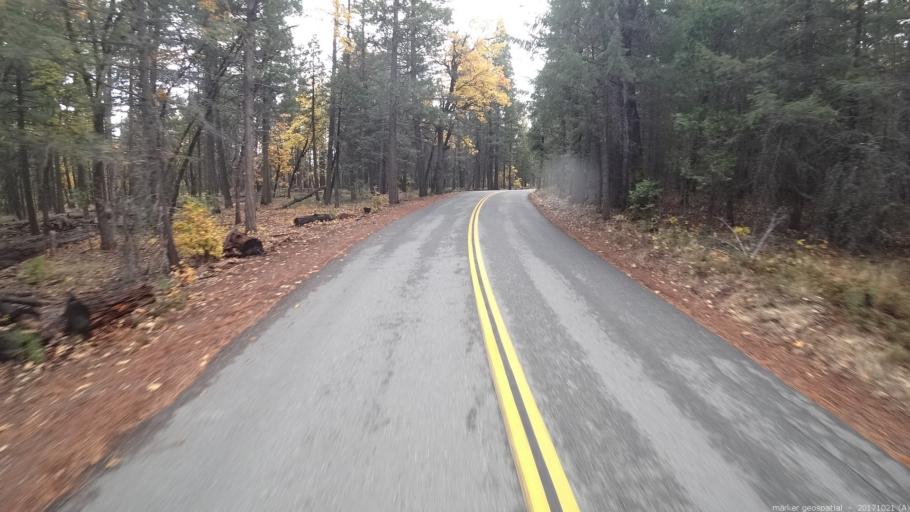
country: US
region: California
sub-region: Shasta County
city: Burney
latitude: 41.0124
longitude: -121.6538
